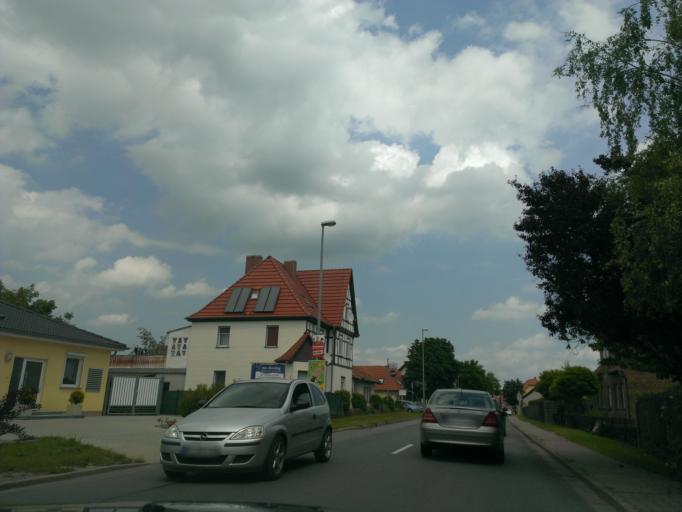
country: DE
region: Thuringia
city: Kleinmolsen
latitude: 51.0056
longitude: 11.0980
